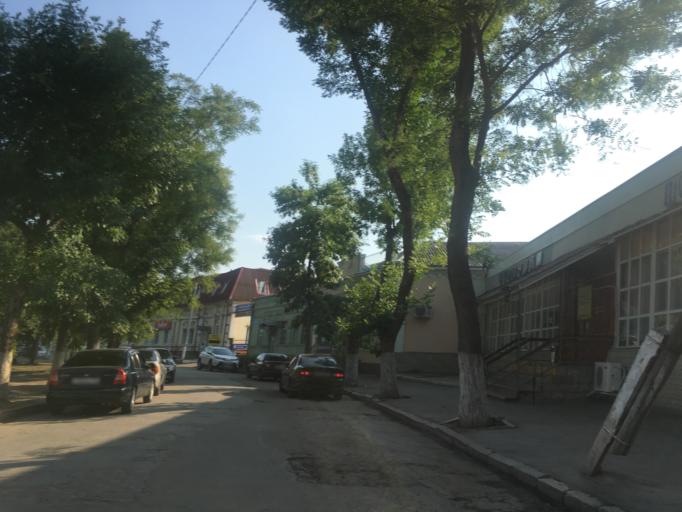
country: RU
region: Krasnodarskiy
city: Yeysk
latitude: 46.7145
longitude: 38.2744
